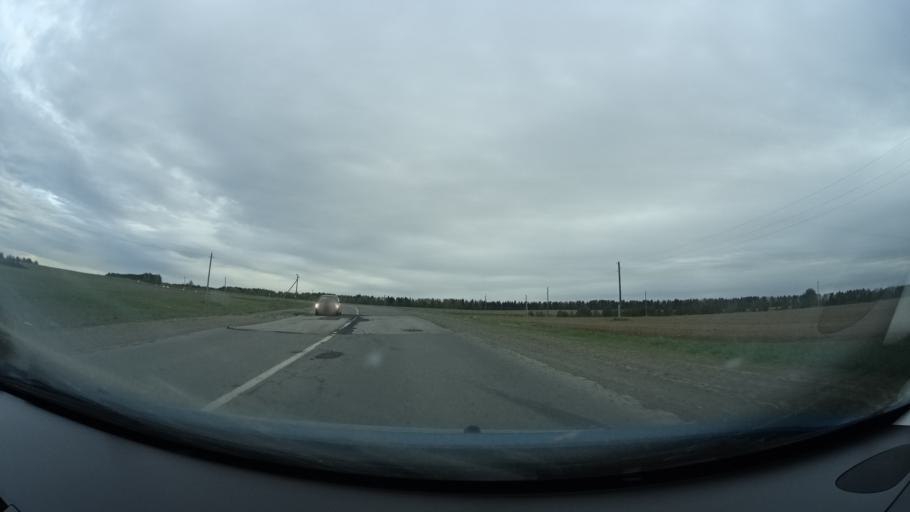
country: RU
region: Perm
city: Osa
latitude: 57.2839
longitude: 55.5671
